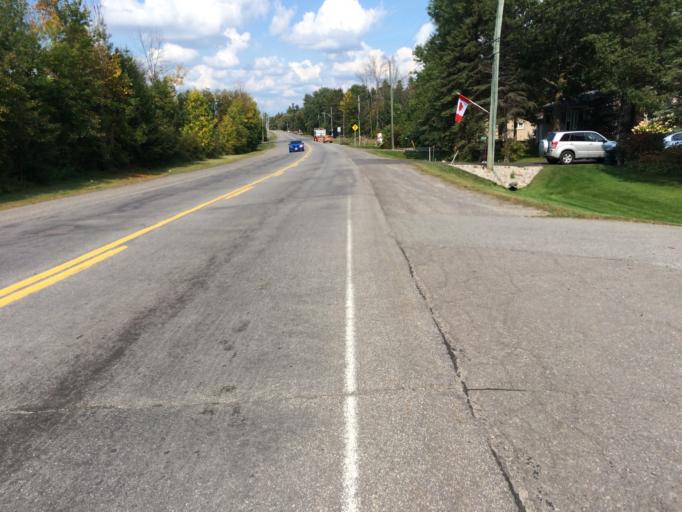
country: CA
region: Ontario
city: Bells Corners
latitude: 45.1666
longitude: -75.6410
